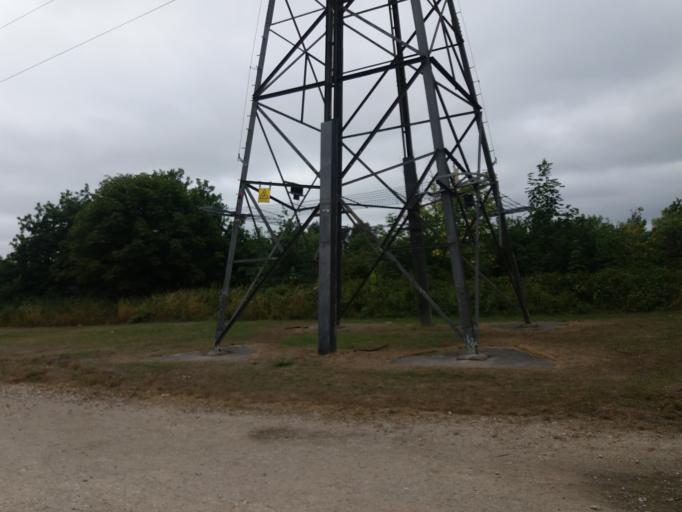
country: GB
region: England
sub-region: Lancashire
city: Preston
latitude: 53.7575
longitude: -2.7320
